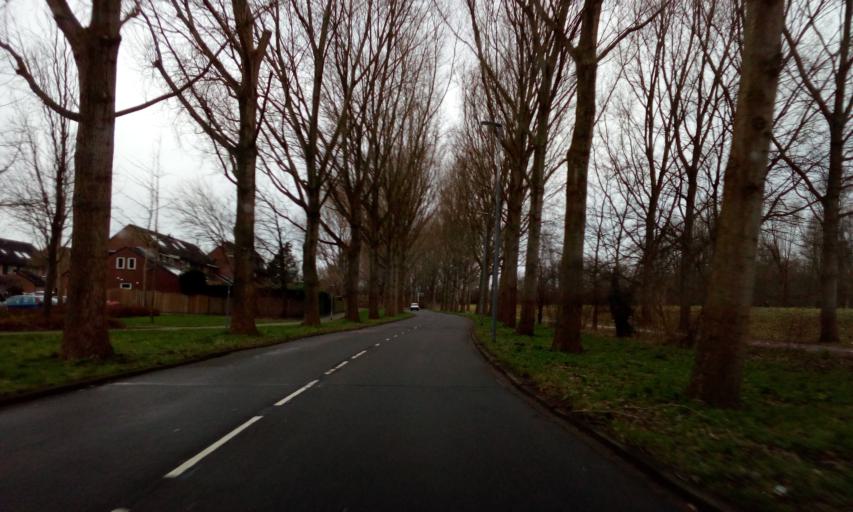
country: NL
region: South Holland
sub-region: Gemeente Lansingerland
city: Bleiswijk
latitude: 51.9699
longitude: 4.5516
